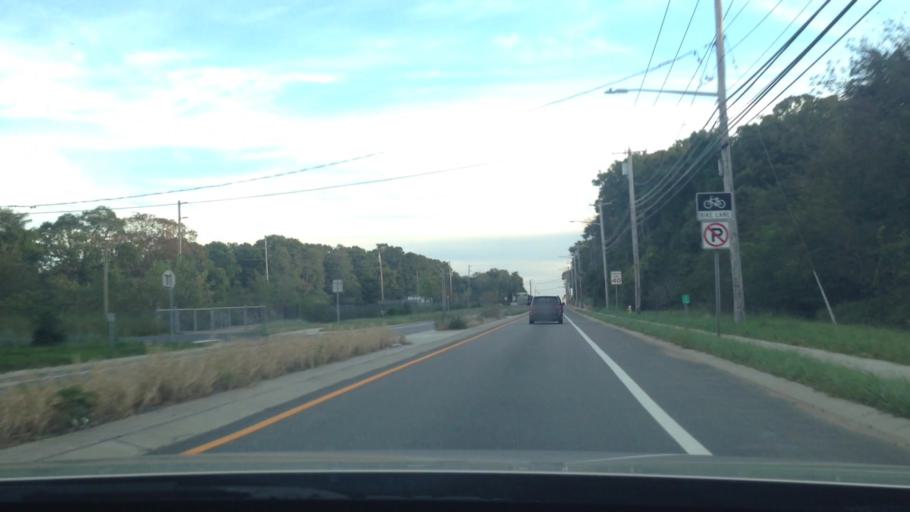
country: US
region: New York
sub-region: Suffolk County
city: Coram
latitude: 40.8538
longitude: -72.9981
